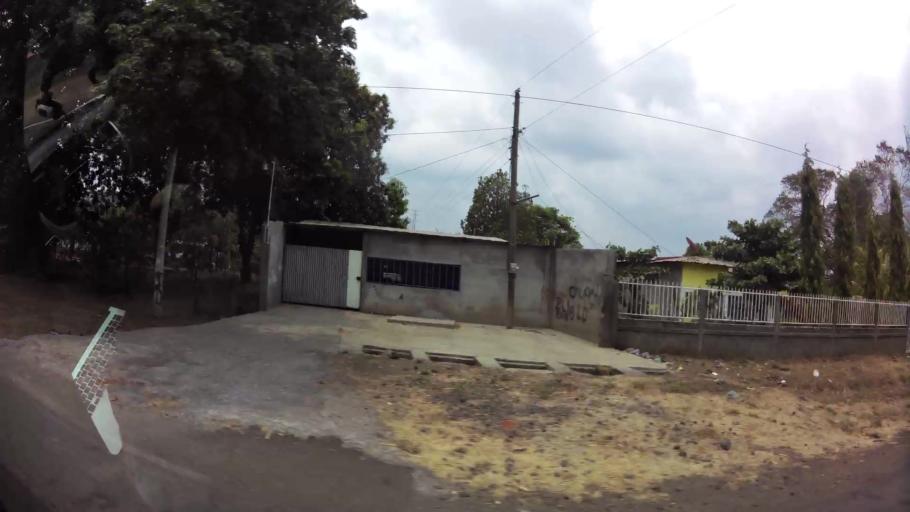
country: NI
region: Leon
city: Quezalguaque
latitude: 12.5299
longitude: -86.8883
